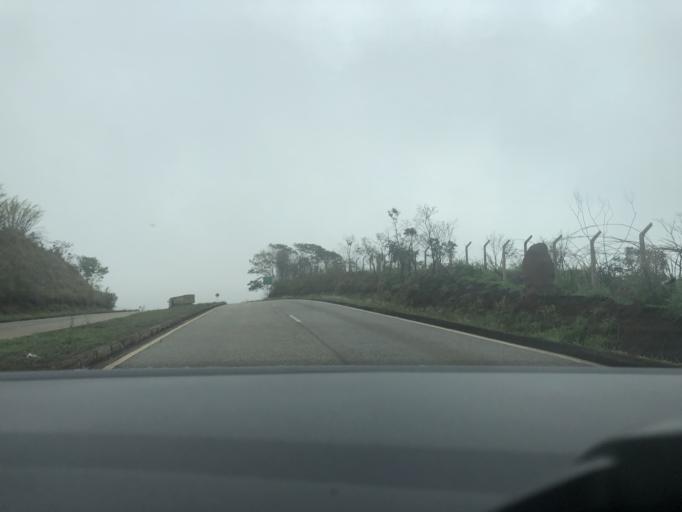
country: BR
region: Minas Gerais
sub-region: Congonhas
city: Congonhas
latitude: -20.5928
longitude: -43.9514
